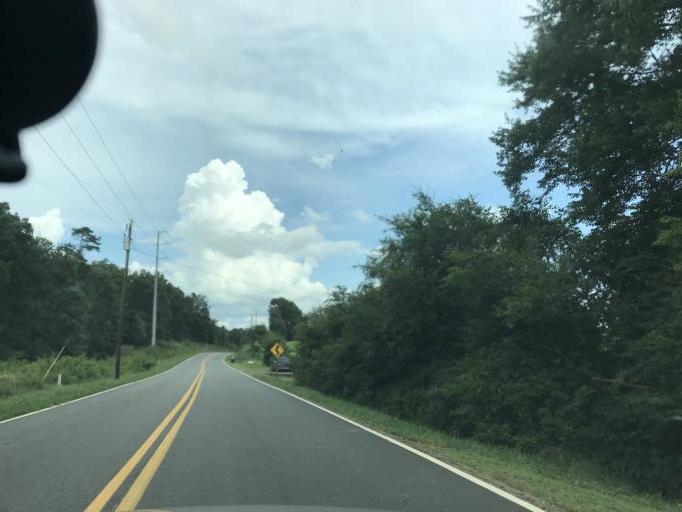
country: US
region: Georgia
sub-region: Cherokee County
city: Ball Ground
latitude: 34.3256
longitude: -84.2496
